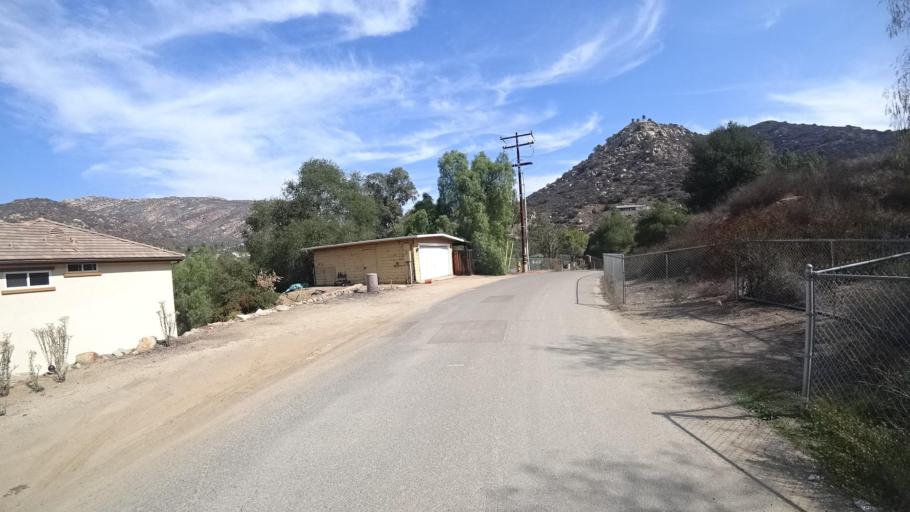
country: US
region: California
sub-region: San Diego County
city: Harbison Canyon
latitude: 32.8139
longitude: -116.8350
